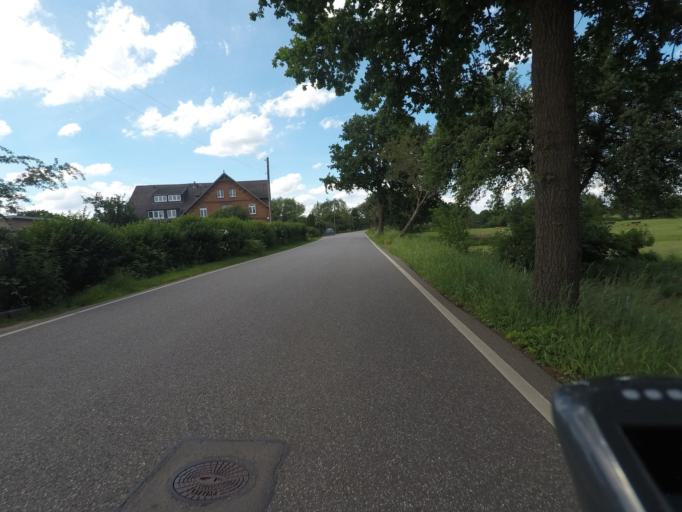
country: DE
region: Lower Saxony
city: Drage
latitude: 53.4339
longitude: 10.2390
